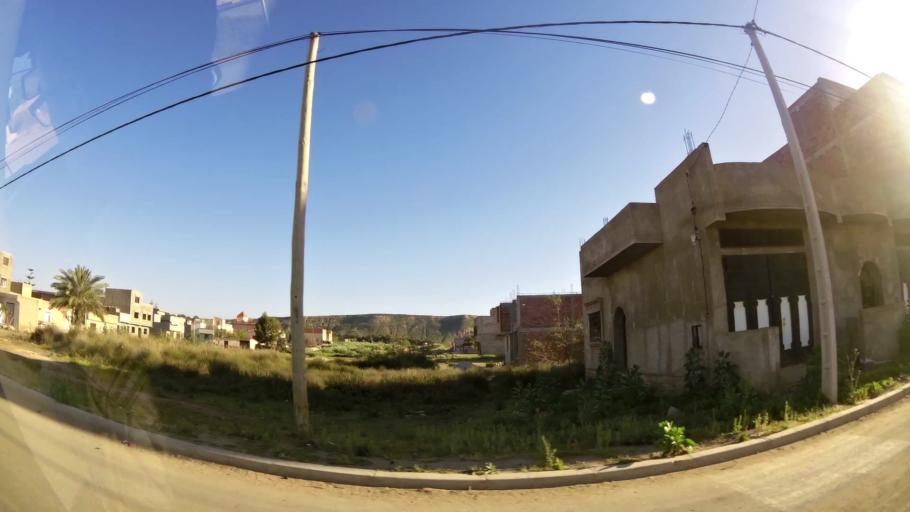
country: MA
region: Oriental
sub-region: Berkane-Taourirt
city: Madagh
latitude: 35.0829
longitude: -2.2521
